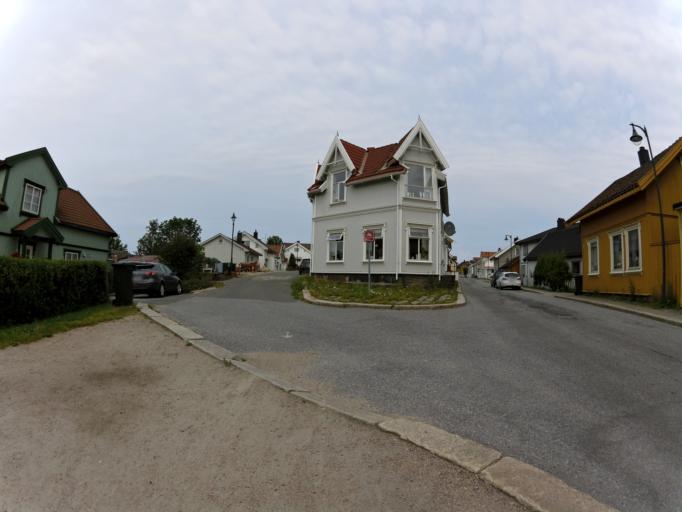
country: NO
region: Ostfold
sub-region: Fredrikstad
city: Fredrikstad
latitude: 59.2135
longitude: 10.9668
